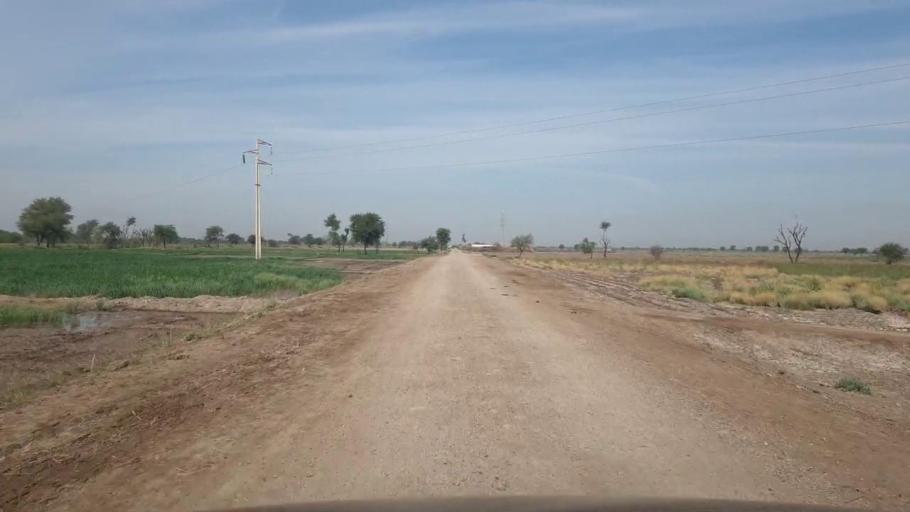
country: PK
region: Sindh
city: Umarkot
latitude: 25.3657
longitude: 69.6509
